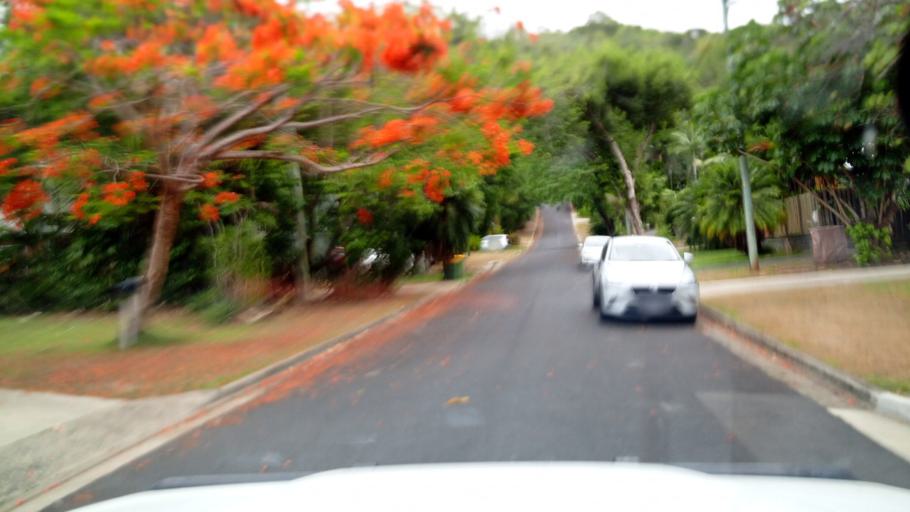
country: AU
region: Queensland
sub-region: Cairns
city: Redlynch
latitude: -16.8791
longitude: 145.7235
